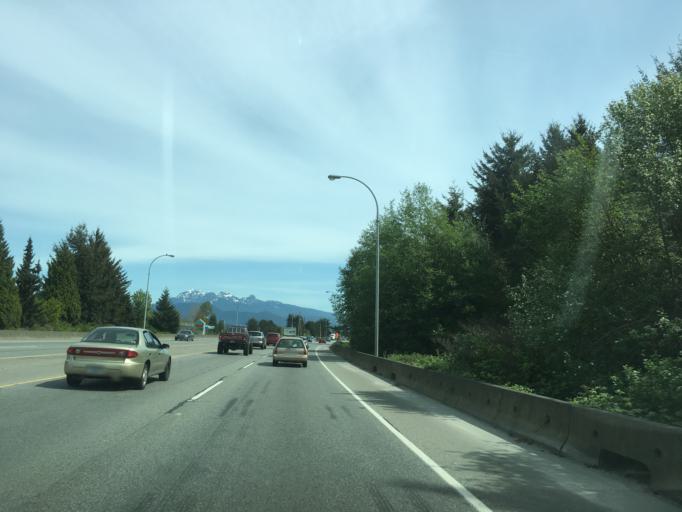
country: CA
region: British Columbia
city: Coquitlam
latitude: 49.2455
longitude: -122.7522
